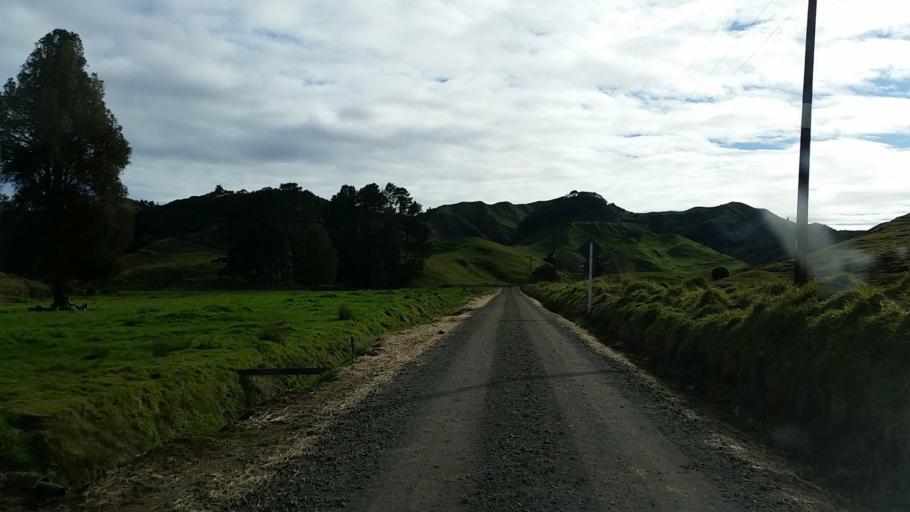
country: NZ
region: Taranaki
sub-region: South Taranaki District
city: Eltham
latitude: -39.2279
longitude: 174.5644
